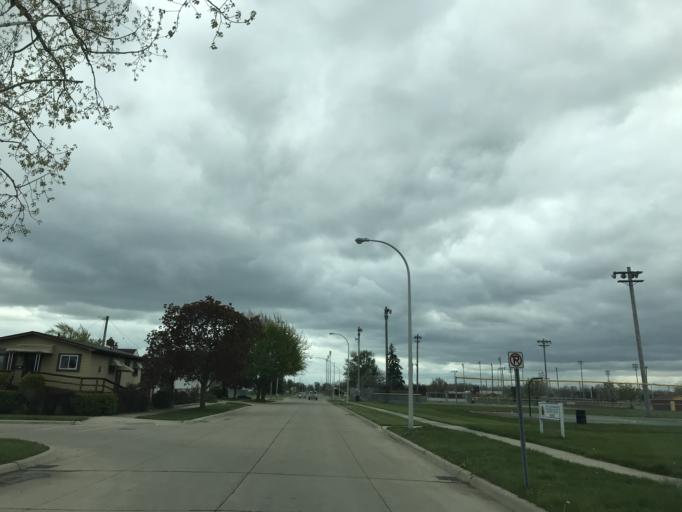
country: US
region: Michigan
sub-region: Wayne County
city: Riverview
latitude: 42.1793
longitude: -83.1744
